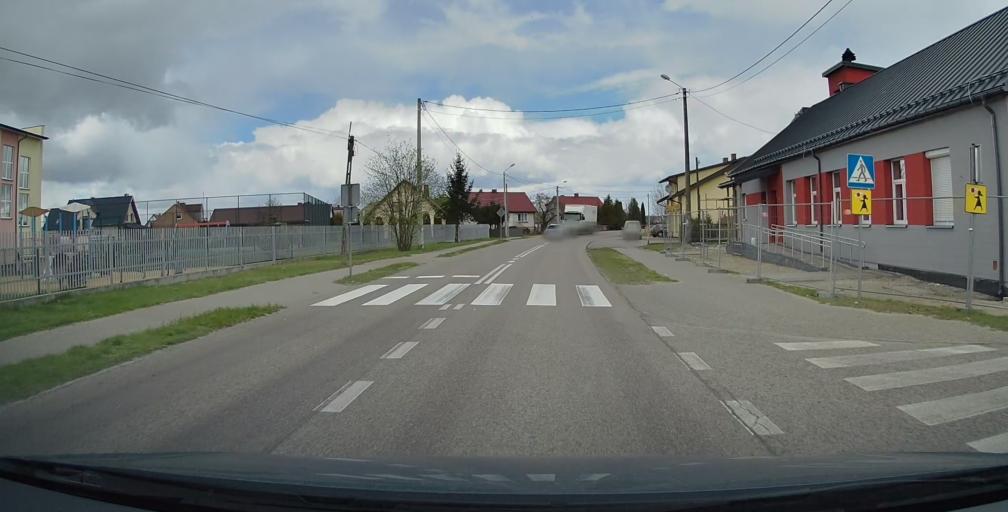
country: PL
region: Masovian Voivodeship
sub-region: Powiat ostrolecki
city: Rzekun
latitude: 52.9958
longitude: 21.5889
